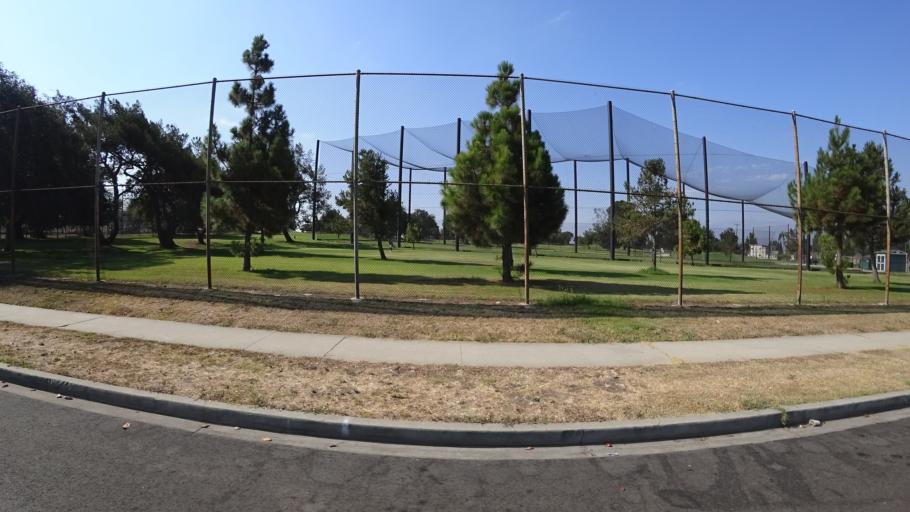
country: US
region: California
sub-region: Los Angeles County
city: Westmont
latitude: 33.9491
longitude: -118.3127
